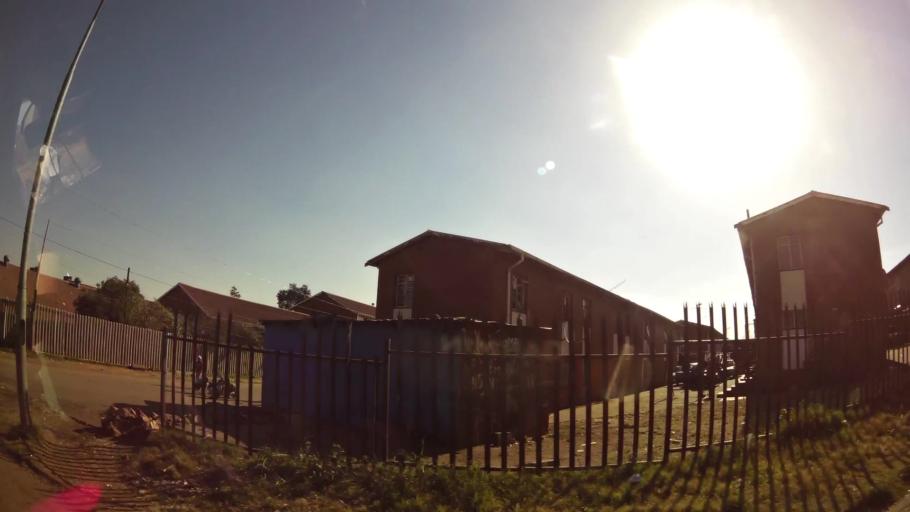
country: ZA
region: Gauteng
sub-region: City of Johannesburg Metropolitan Municipality
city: Johannesburg
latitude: -26.1937
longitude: 27.9774
